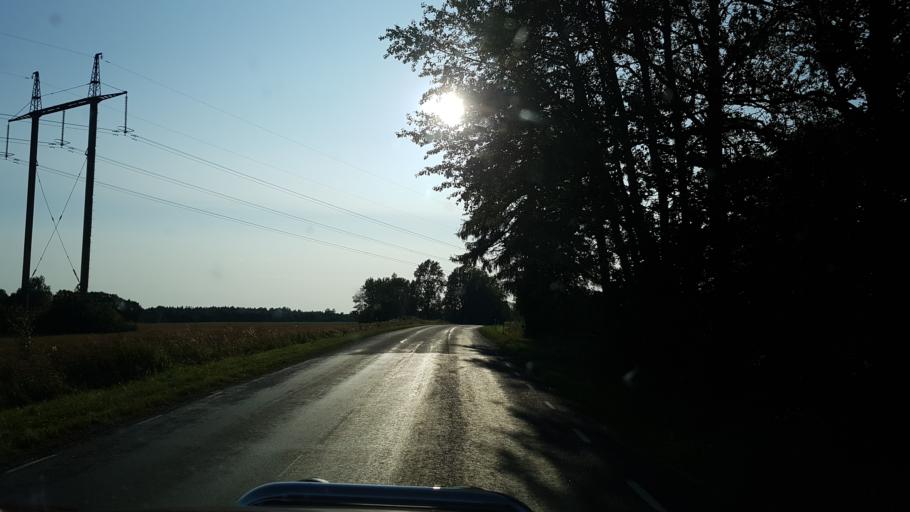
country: EE
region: Raplamaa
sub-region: Kehtna vald
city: Kehtna
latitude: 59.0544
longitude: 24.9973
